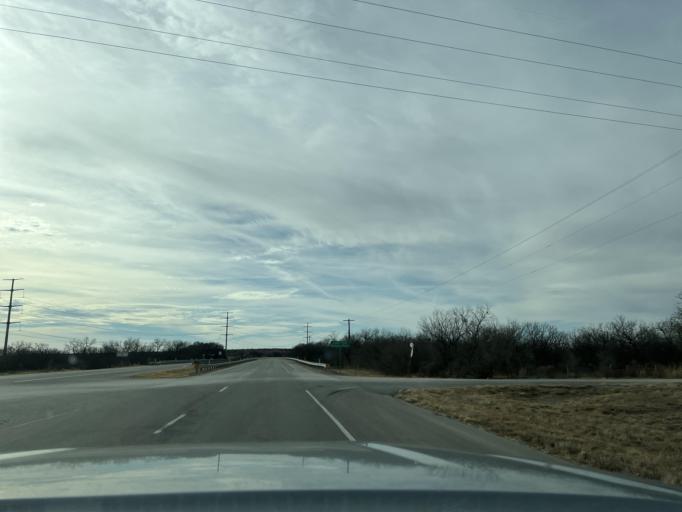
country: US
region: Texas
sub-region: Jones County
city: Stamford
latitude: 32.7526
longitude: -99.6233
